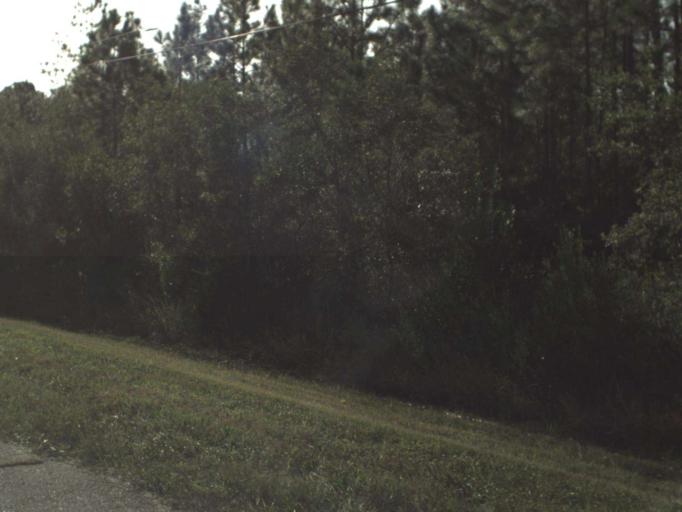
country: US
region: Florida
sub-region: Escambia County
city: Myrtle Grove
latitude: 30.3345
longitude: -87.4121
